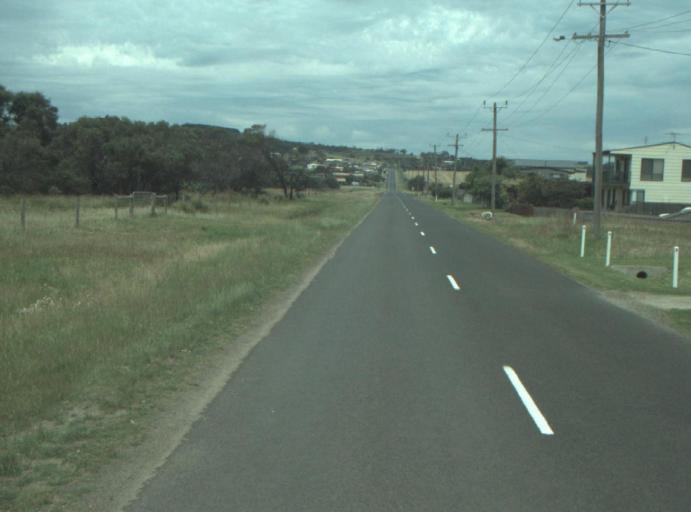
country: AU
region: Victoria
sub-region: Greater Geelong
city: Clifton Springs
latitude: -38.1132
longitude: 144.6292
